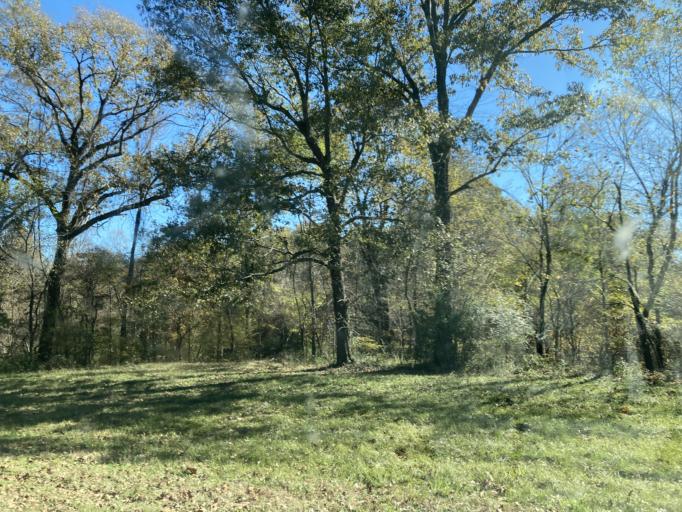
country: US
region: Mississippi
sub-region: Hinds County
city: Lynchburg
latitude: 32.5775
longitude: -90.5722
